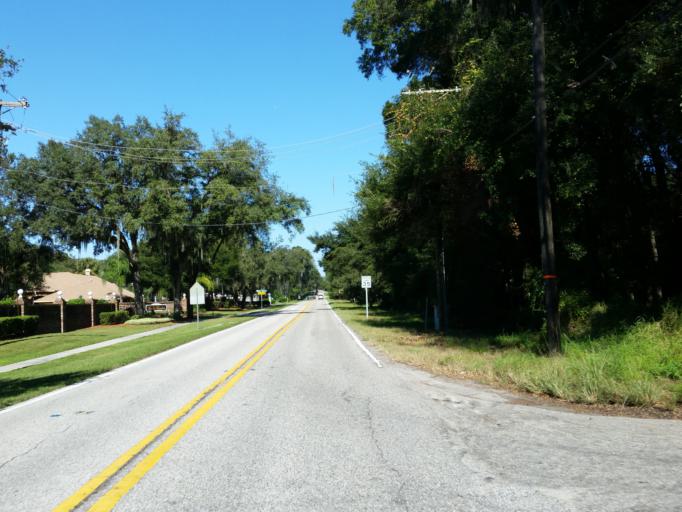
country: US
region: Florida
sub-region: Hillsborough County
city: Bloomingdale
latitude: 27.9009
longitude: -82.2692
